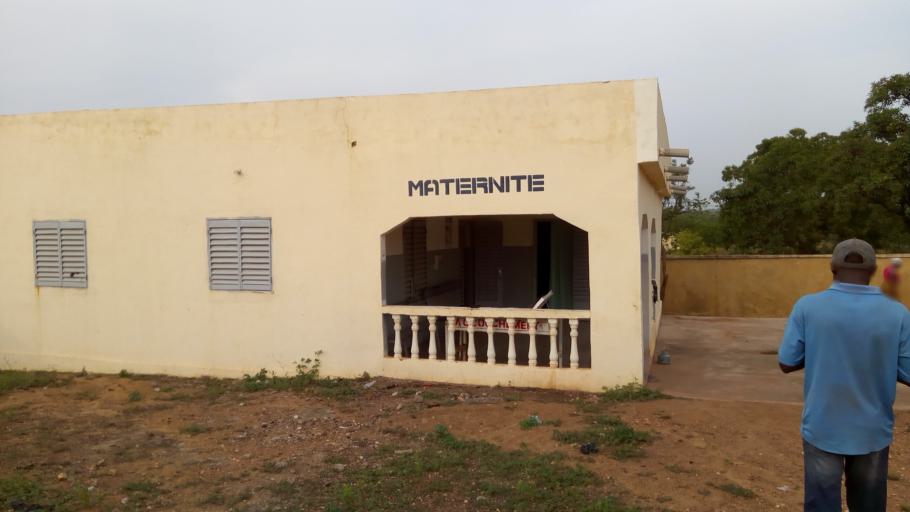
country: ML
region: Koulikoro
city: Kangaba
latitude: 11.6768
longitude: -8.6521
